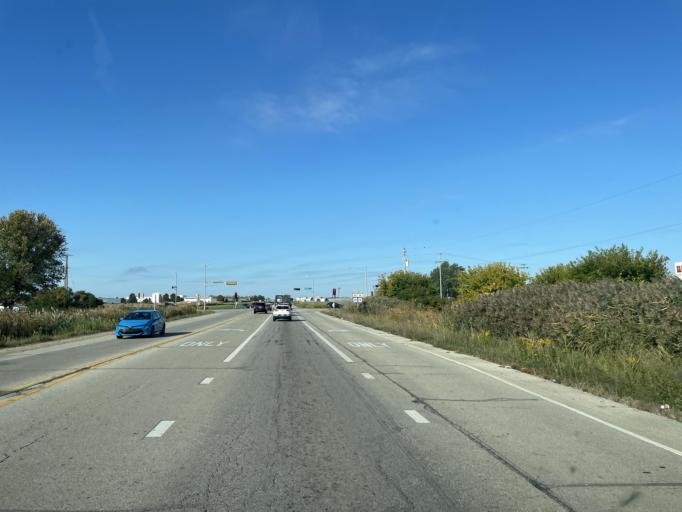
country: US
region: Wisconsin
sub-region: Kenosha County
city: Pleasant Prairie
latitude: 42.5892
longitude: -87.9133
